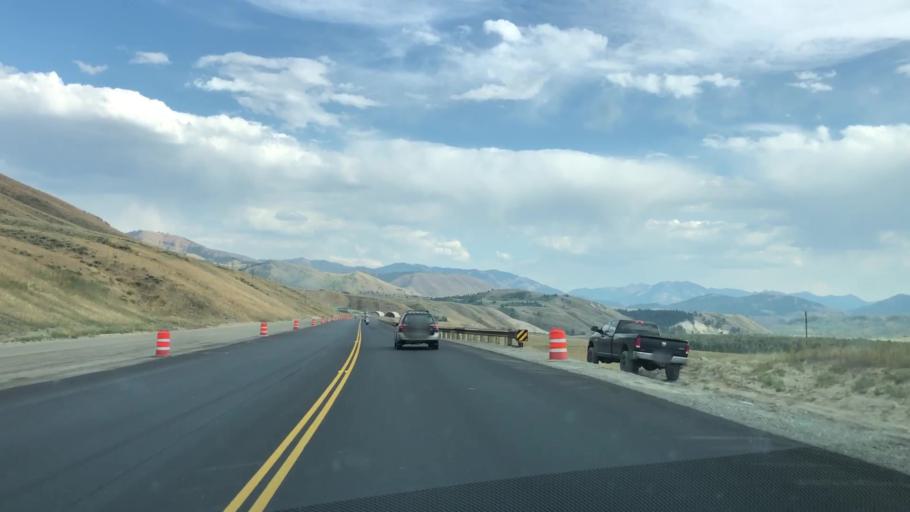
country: US
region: Wyoming
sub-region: Teton County
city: South Park
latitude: 43.4099
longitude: -110.7684
